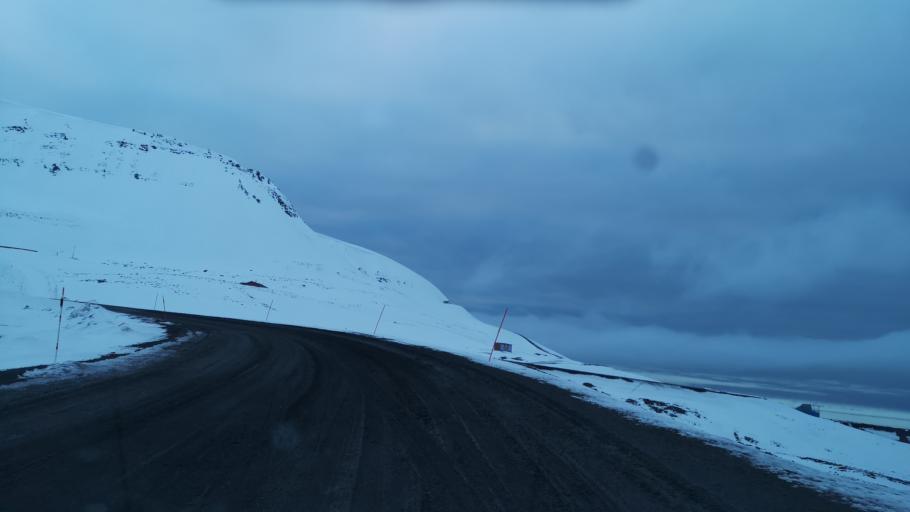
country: SJ
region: Svalbard
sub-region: Spitsbergen
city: Longyearbyen
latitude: 78.2355
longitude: 15.4661
